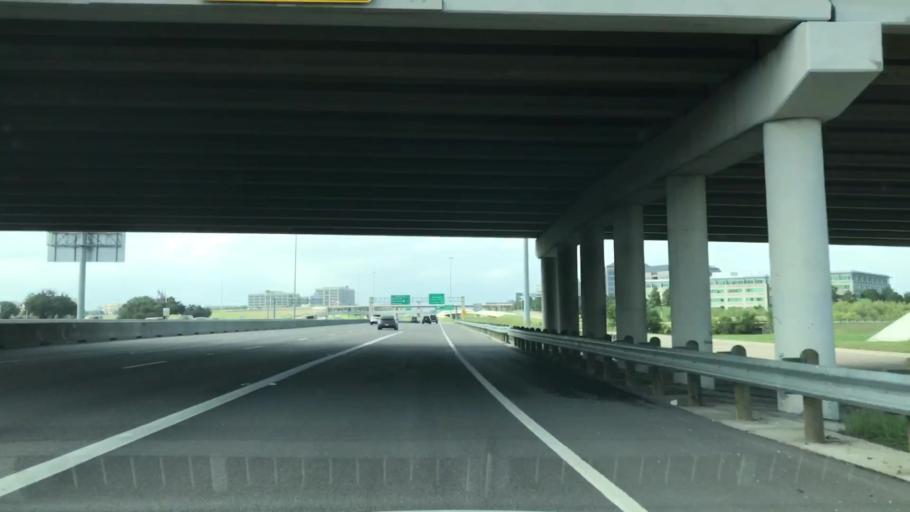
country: US
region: Texas
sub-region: Dallas County
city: Farmers Branch
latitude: 32.8904
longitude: -96.9623
